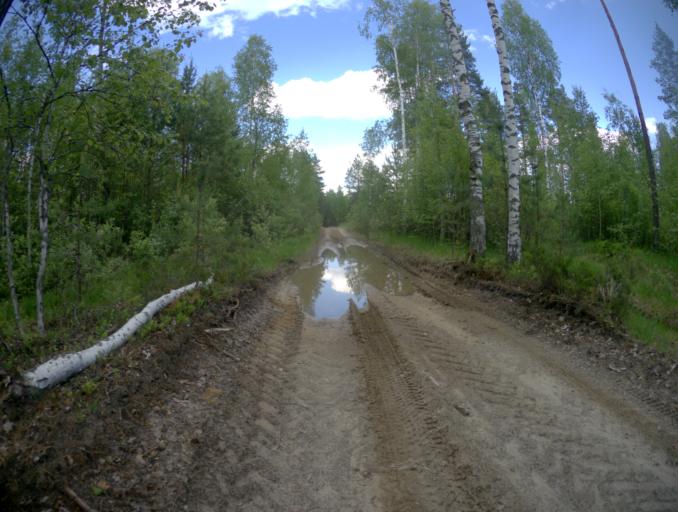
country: RU
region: Vladimir
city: Zolotkovo
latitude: 55.3291
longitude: 40.9542
